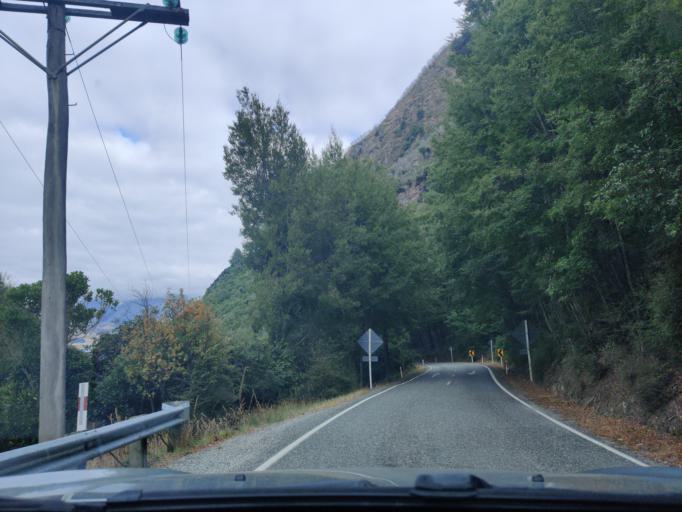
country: NZ
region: Otago
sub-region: Queenstown-Lakes District
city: Queenstown
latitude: -45.0790
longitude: 168.4851
